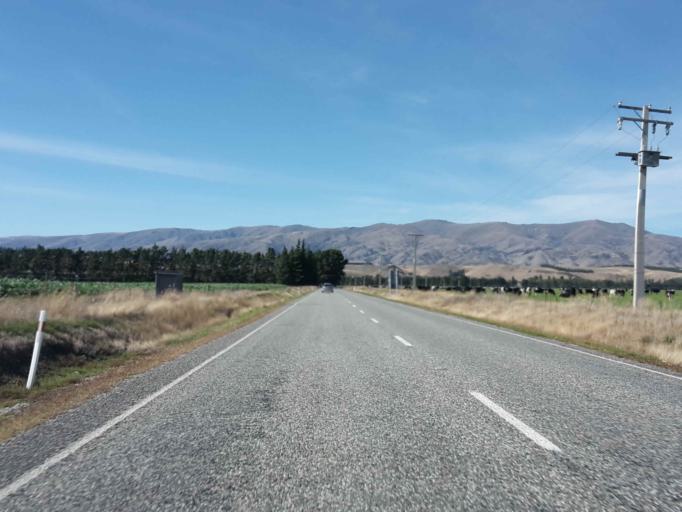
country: NZ
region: Otago
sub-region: Queenstown-Lakes District
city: Wanaka
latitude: -44.8247
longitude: 169.3571
